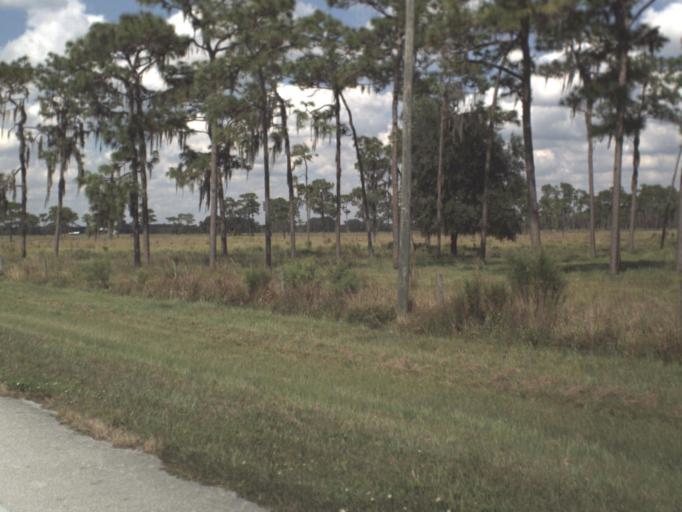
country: US
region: Florida
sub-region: Highlands County
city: Sebring
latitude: 27.4293
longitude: -81.5898
